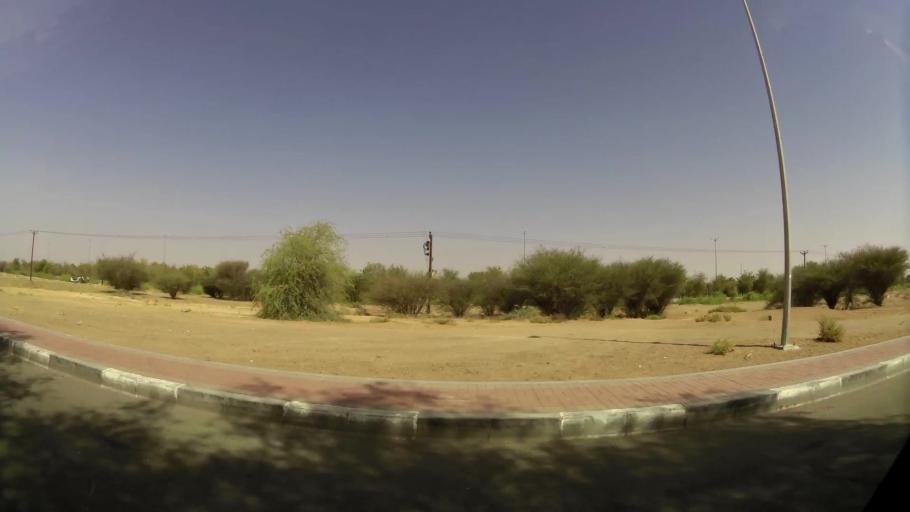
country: OM
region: Al Buraimi
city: Al Buraymi
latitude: 24.3020
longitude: 55.7930
